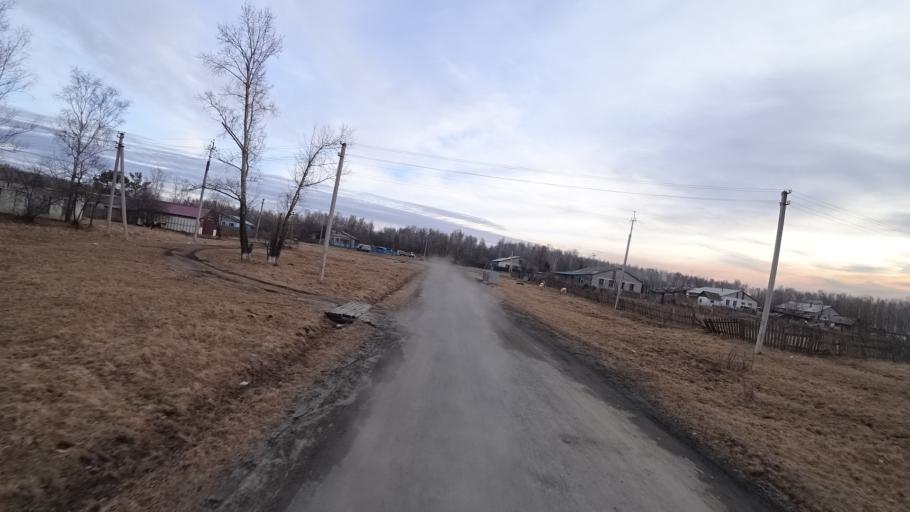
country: RU
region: Amur
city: Bureya
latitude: 50.0165
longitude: 129.7680
